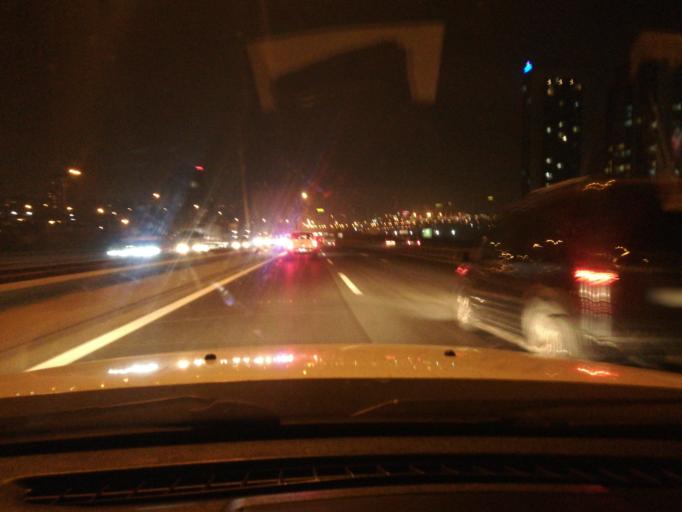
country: TR
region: Istanbul
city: Esenyurt
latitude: 41.0557
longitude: 28.6847
